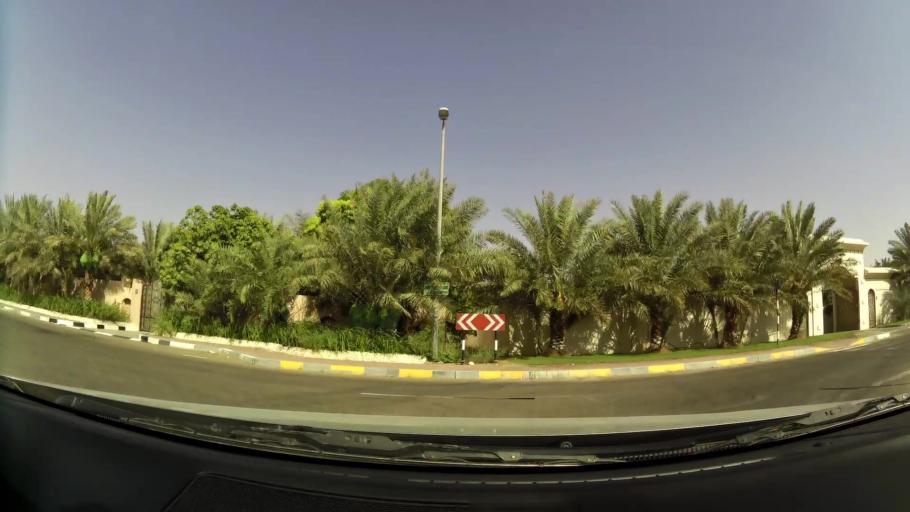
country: OM
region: Al Buraimi
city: Al Buraymi
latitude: 24.3369
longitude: 55.7913
